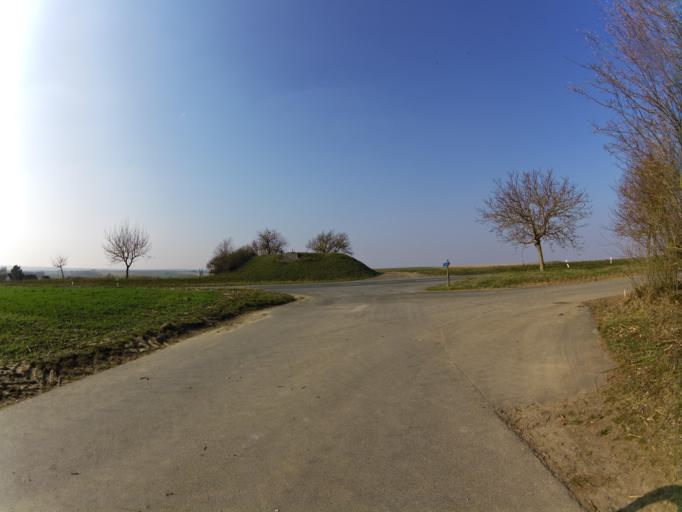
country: DE
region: Bavaria
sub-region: Regierungsbezirk Unterfranken
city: Eibelstadt
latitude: 49.6994
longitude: 9.9792
